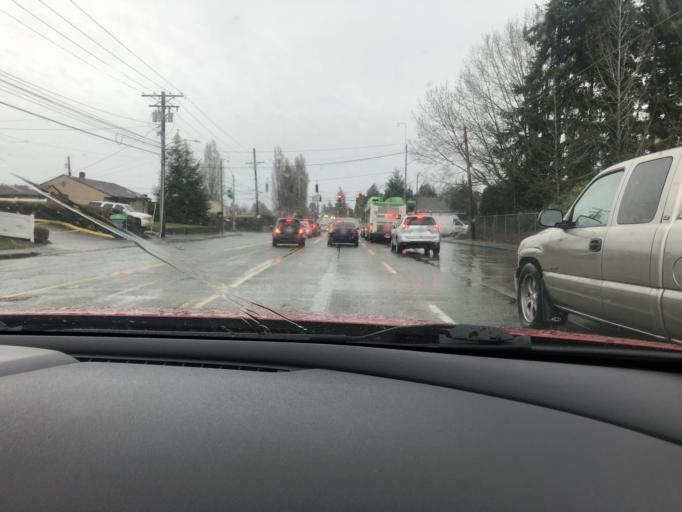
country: US
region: Washington
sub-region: Pierce County
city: Tacoma
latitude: 47.2427
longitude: -122.4640
